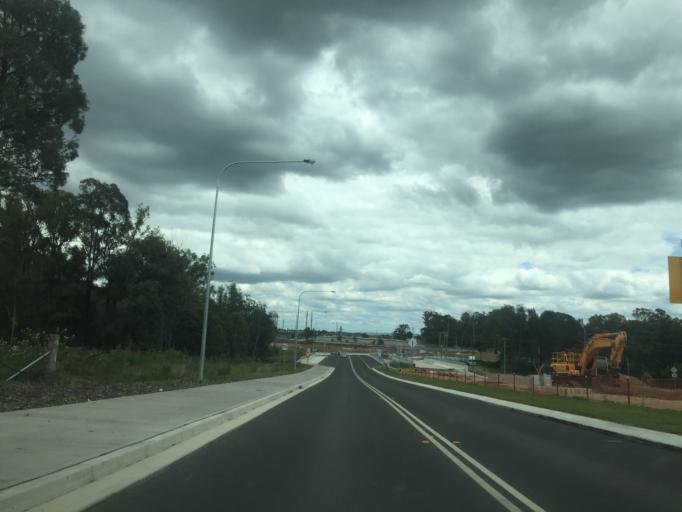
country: AU
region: New South Wales
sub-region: Blacktown
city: Riverstone
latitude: -33.7006
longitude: 150.8761
